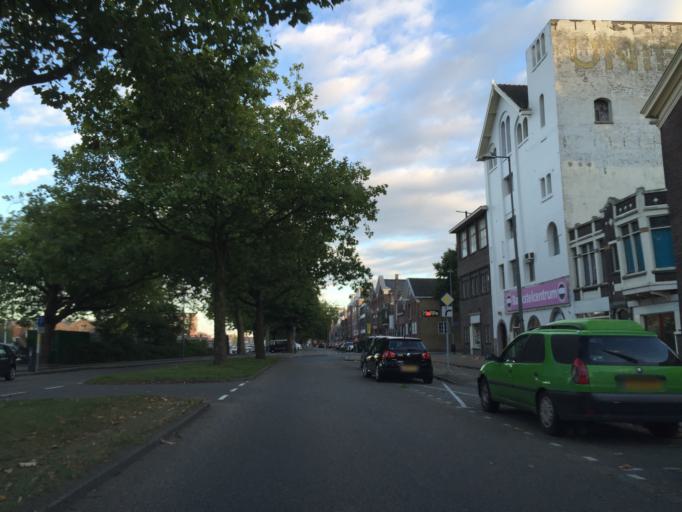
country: NL
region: South Holland
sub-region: Gemeente Schiedam
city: Schiedam
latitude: 51.9119
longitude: 4.3995
